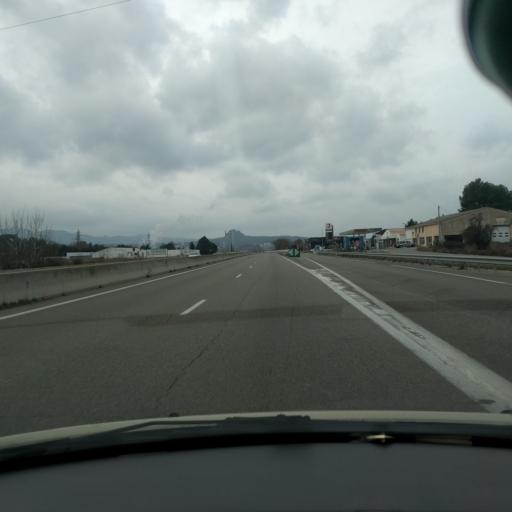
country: FR
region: Provence-Alpes-Cote d'Azur
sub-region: Departement des Bouches-du-Rhone
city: Gardanne
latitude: 43.4691
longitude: 5.4687
